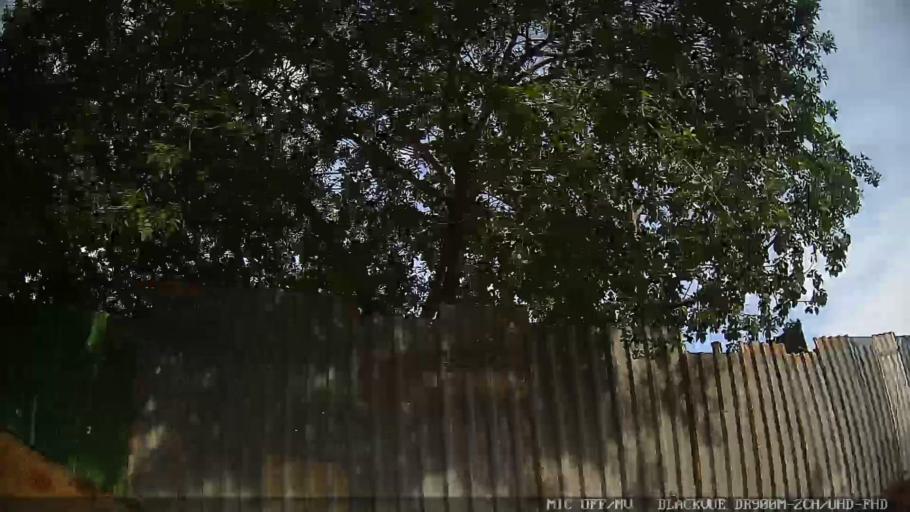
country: BR
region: Sao Paulo
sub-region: Braganca Paulista
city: Braganca Paulista
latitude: -22.9188
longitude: -46.5484
